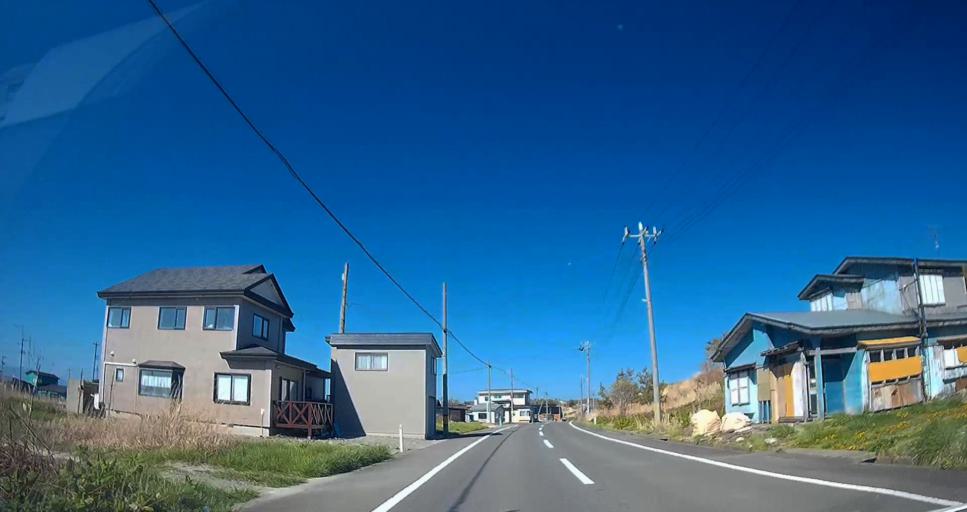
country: JP
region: Hokkaido
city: Hakodate
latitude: 41.5395
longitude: 140.9105
